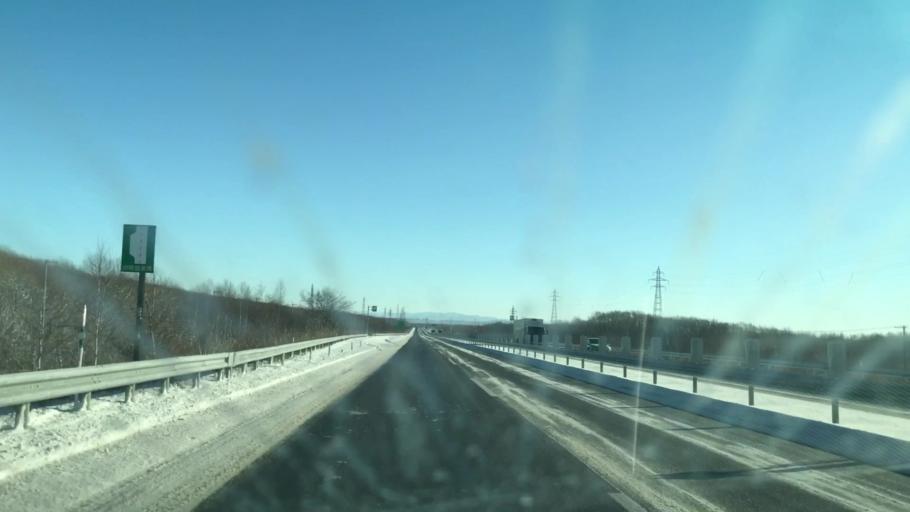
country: JP
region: Hokkaido
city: Tomakomai
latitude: 42.6737
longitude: 141.7490
